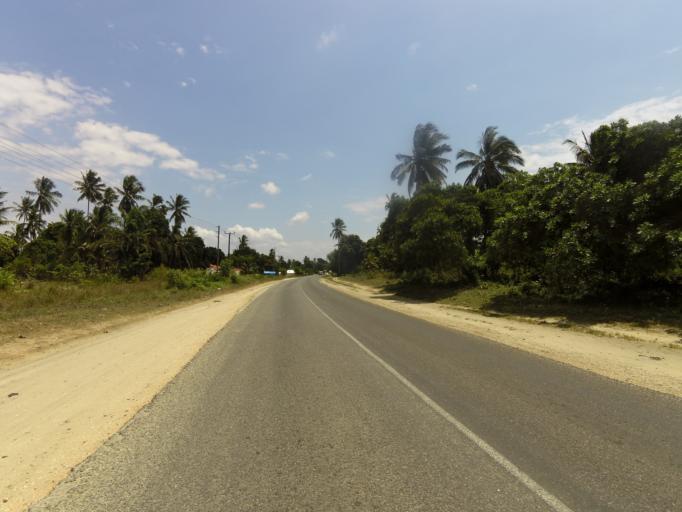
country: TZ
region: Pwani
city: Vikindu
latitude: -7.0324
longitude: 39.2906
